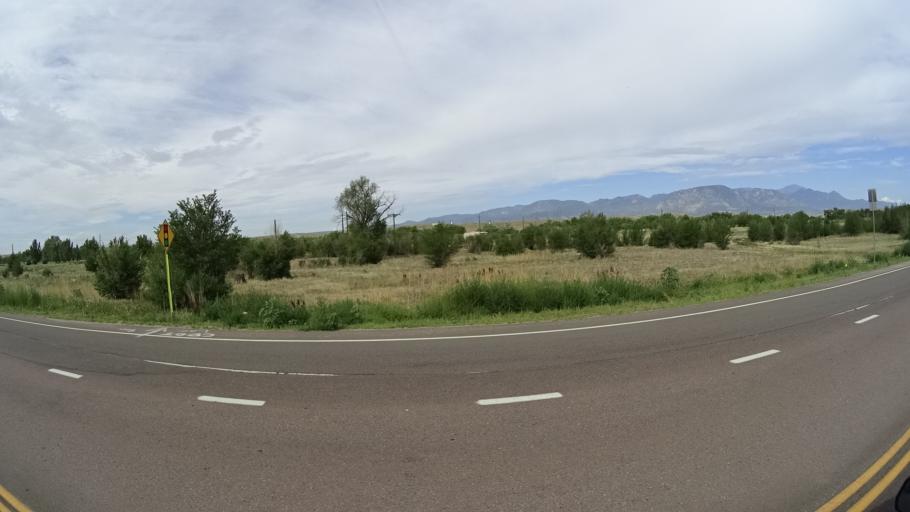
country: US
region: Colorado
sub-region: El Paso County
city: Fountain
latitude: 38.7111
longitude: -104.7121
